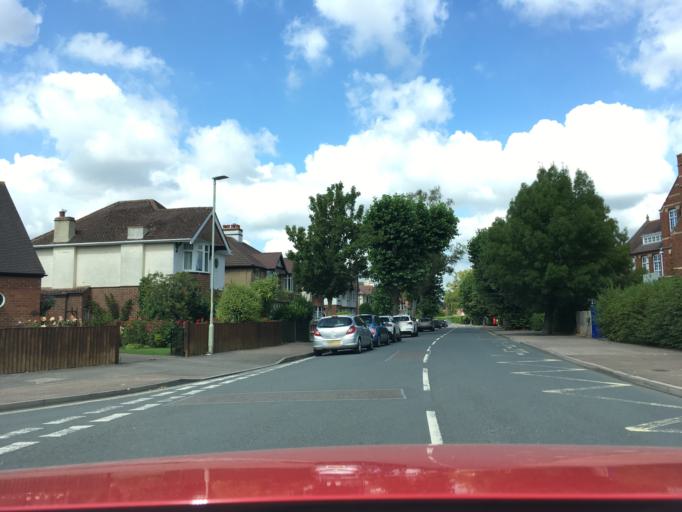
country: GB
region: England
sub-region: Gloucestershire
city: Gloucester
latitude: 51.8721
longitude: -2.2362
